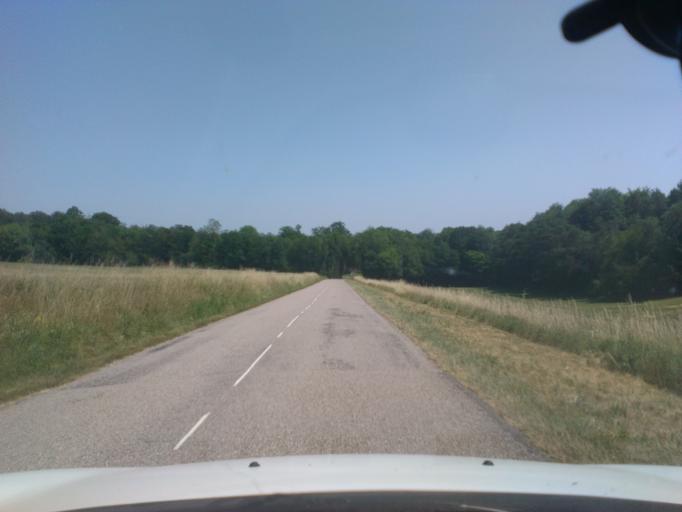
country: FR
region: Lorraine
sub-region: Departement des Vosges
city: Liffol-le-Grand
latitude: 48.4134
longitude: 5.5798
